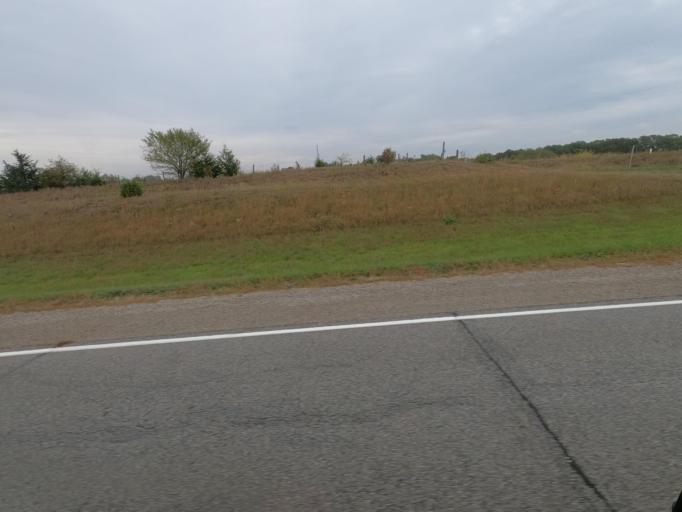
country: US
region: Iowa
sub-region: Van Buren County
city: Keosauqua
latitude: 40.8464
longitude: -92.0307
